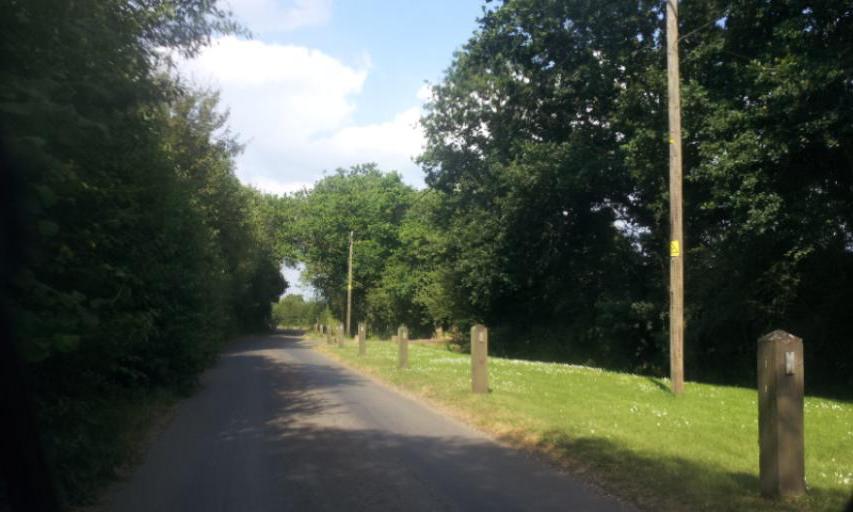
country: GB
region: England
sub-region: Kent
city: Yalding
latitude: 51.1936
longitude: 0.4214
